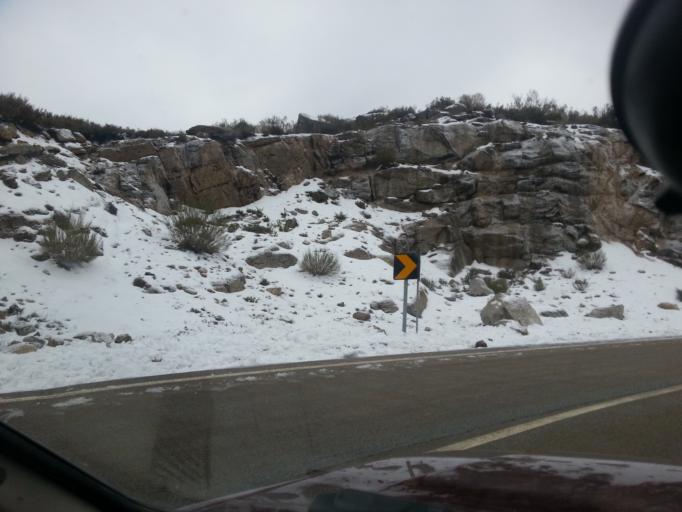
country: PT
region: Guarda
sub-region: Seia
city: Seia
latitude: 40.3585
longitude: -7.6636
